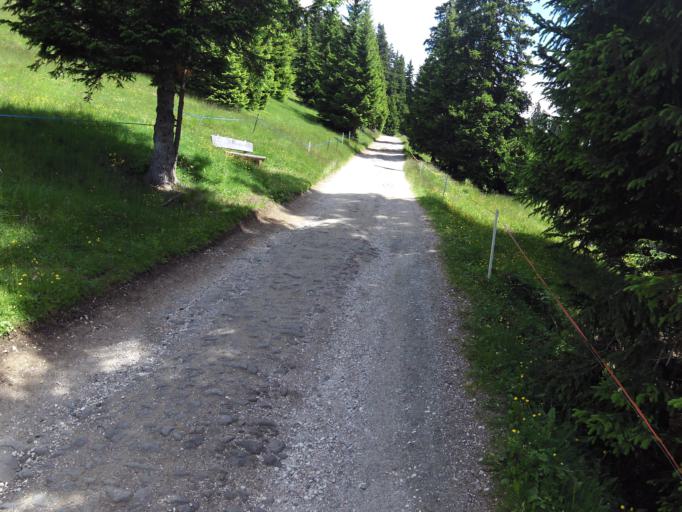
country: IT
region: Trentino-Alto Adige
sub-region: Bolzano
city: Ortisei
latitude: 46.5560
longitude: 11.6643
